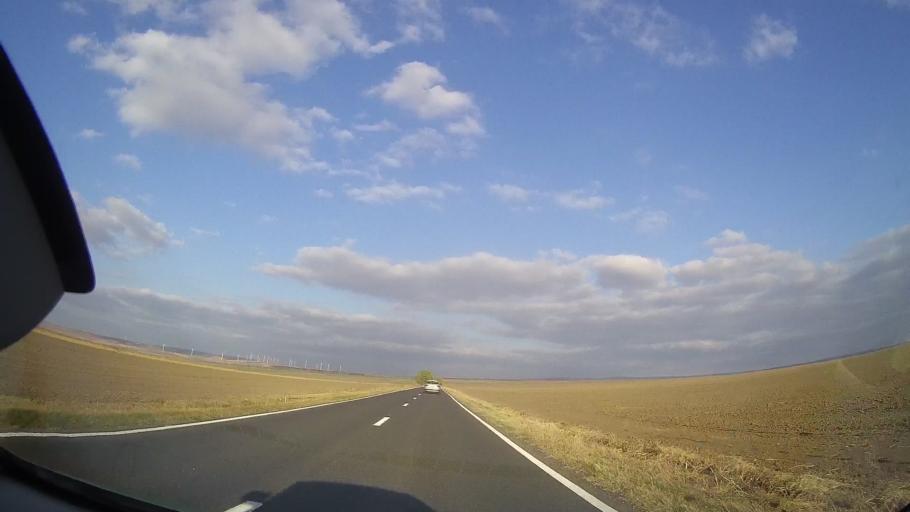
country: RO
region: Tulcea
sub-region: Comuna Topolog
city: Topolog
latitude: 44.8349
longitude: 28.2925
